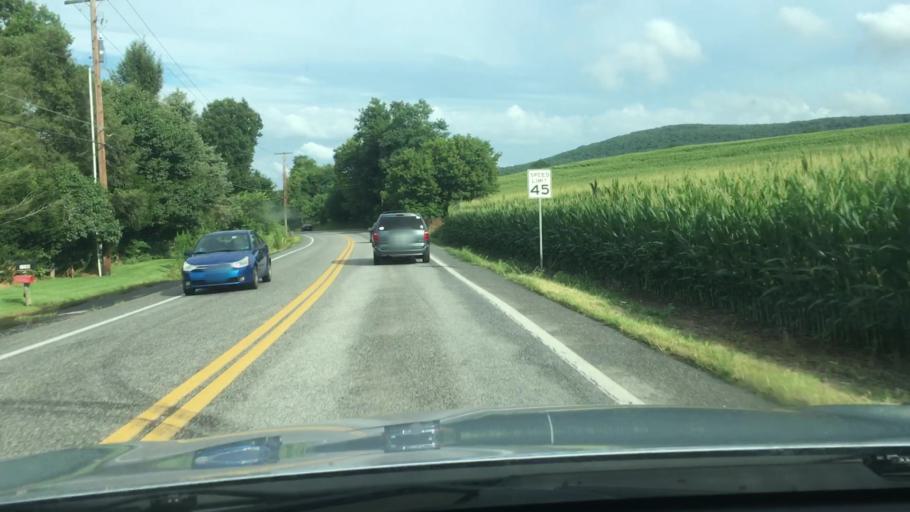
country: US
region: Pennsylvania
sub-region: Cumberland County
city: Boiling Springs
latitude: 40.1510
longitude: -77.0756
